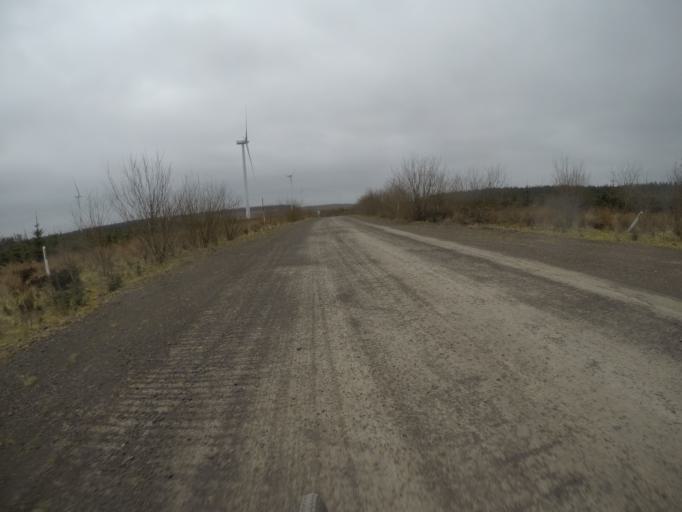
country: GB
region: Scotland
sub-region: East Ayrshire
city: Newmilns
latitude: 55.6516
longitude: -4.3251
